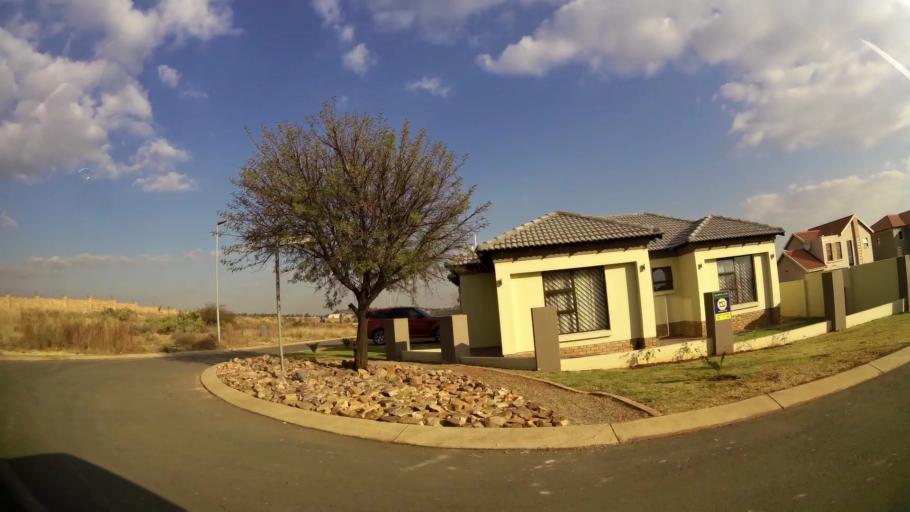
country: ZA
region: Gauteng
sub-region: West Rand District Municipality
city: Krugersdorp
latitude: -26.1015
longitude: 27.7327
